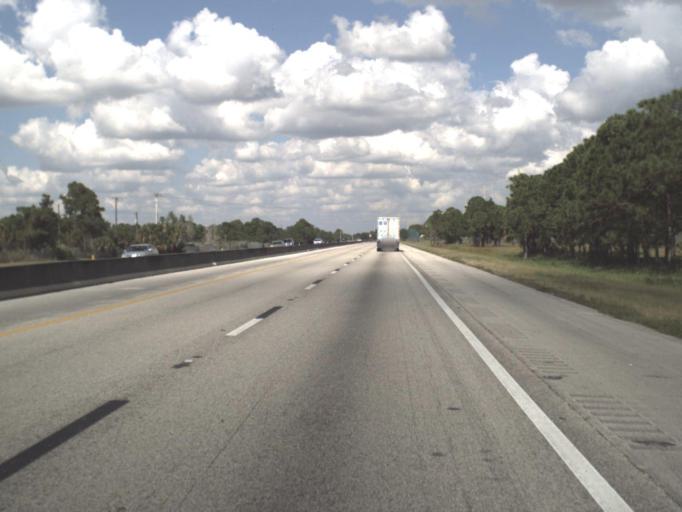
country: US
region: Florida
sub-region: Saint Lucie County
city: Port Saint Lucie
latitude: 27.2475
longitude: -80.3469
